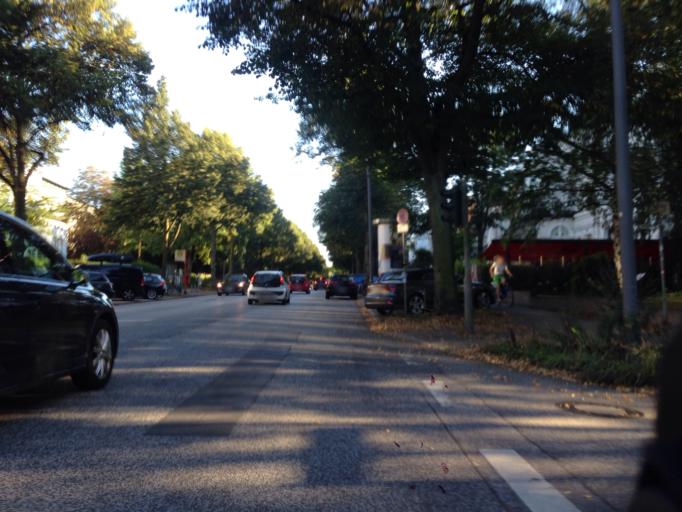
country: DE
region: Hamburg
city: Eimsbuettel
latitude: 53.5776
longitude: 9.9889
